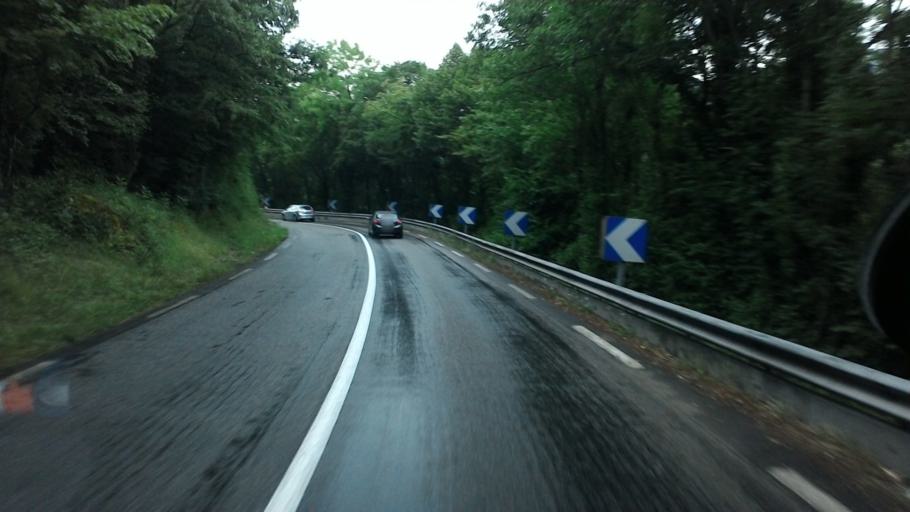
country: FR
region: Rhone-Alpes
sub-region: Departement de la Savoie
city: Le Bourget-du-Lac
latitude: 45.6925
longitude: 5.8323
